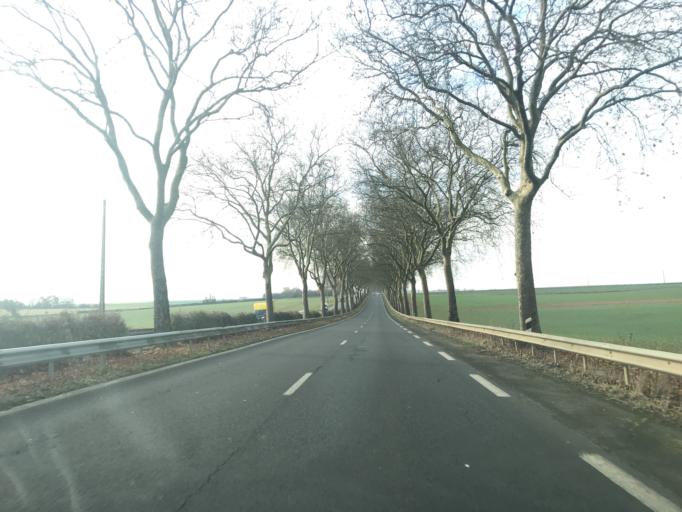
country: FR
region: Poitou-Charentes
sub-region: Departement des Deux-Sevres
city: Chauray
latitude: 46.3491
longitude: -0.3480
